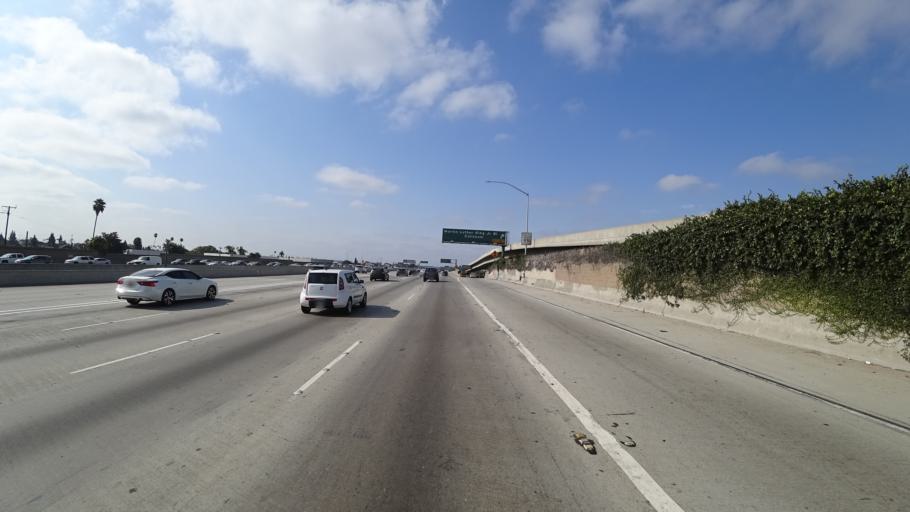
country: US
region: California
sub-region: Los Angeles County
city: Los Angeles
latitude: 34.0142
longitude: -118.2814
